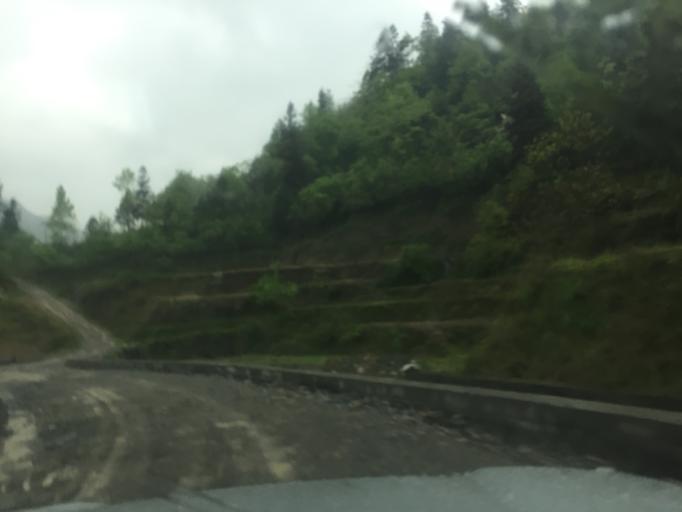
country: CN
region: Guizhou Sheng
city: Changfeng
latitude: 28.4300
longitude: 108.0810
